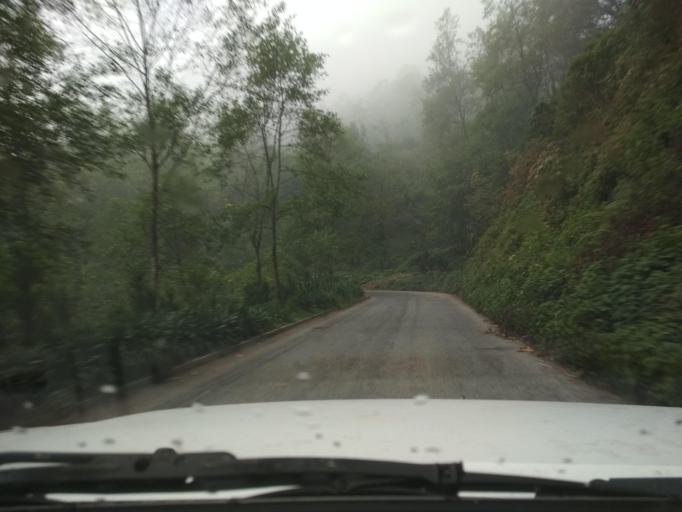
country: MX
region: Veracruz
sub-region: La Perla
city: Metlac Hernandez (Metlac Primero)
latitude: 18.9516
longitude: -97.1702
